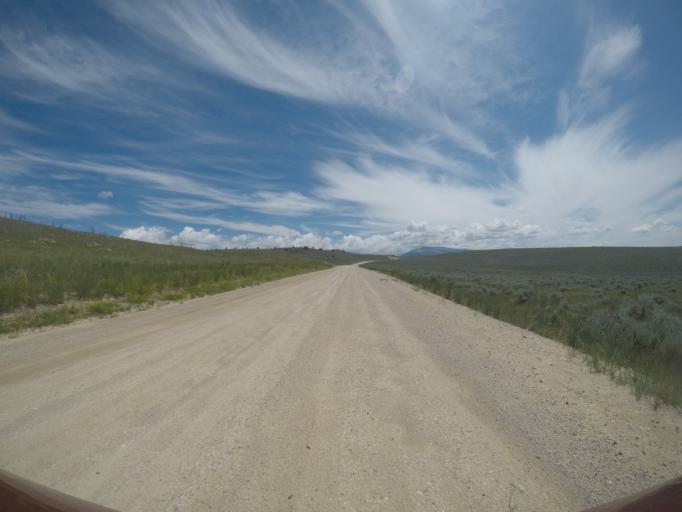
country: US
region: Wyoming
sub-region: Park County
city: Powell
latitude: 45.2065
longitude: -108.7881
